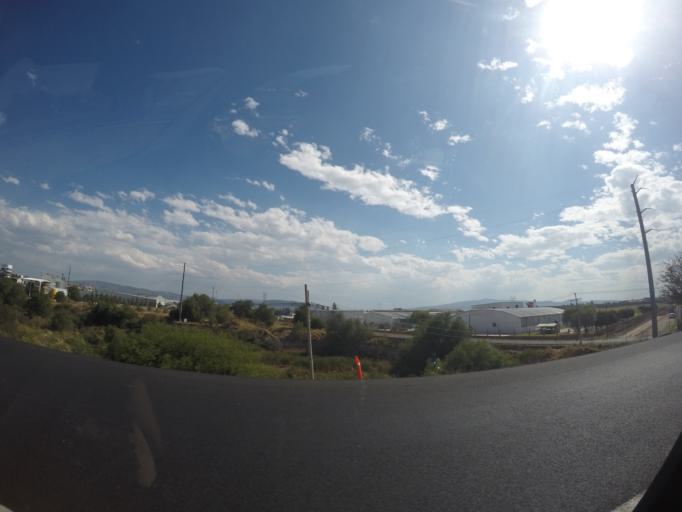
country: MX
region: Guanajuato
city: San Miguel Octopan
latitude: 20.5471
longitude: -100.7507
